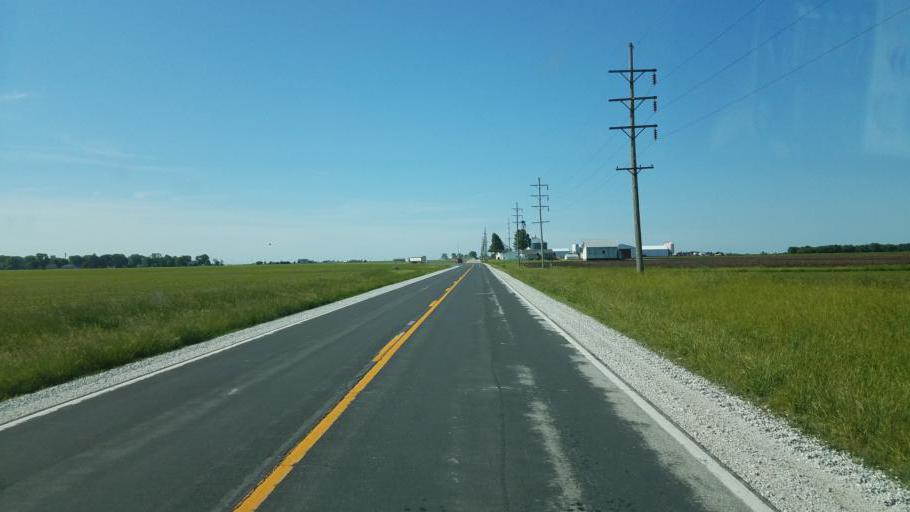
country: US
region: Illinois
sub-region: McDonough County
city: Bushnell
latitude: 40.4288
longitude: -90.5061
